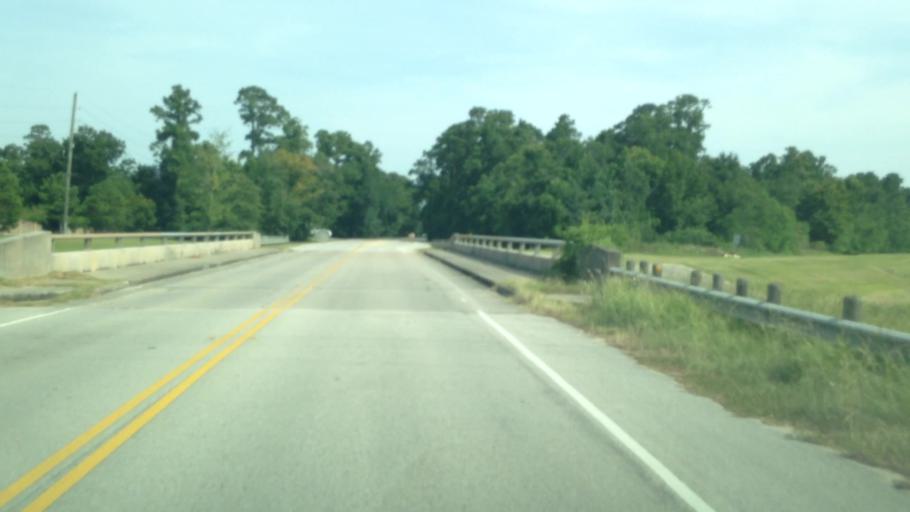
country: US
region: Texas
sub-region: Harris County
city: Sheldon
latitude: 29.9206
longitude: -95.1656
